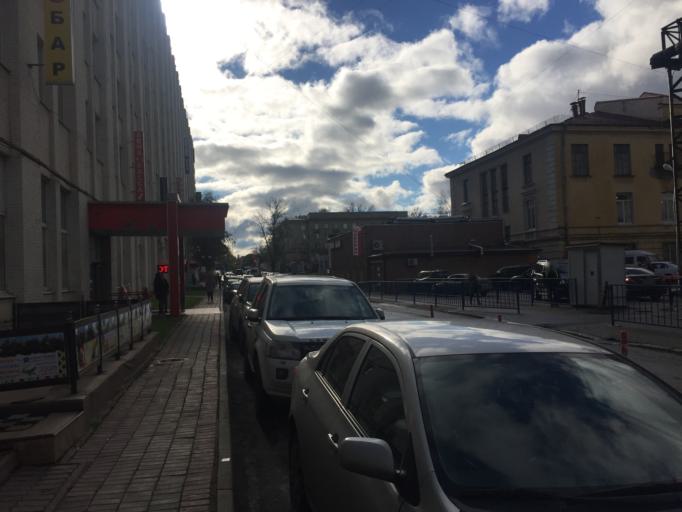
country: RU
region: St.-Petersburg
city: Obukhovo
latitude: 59.8663
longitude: 30.4721
